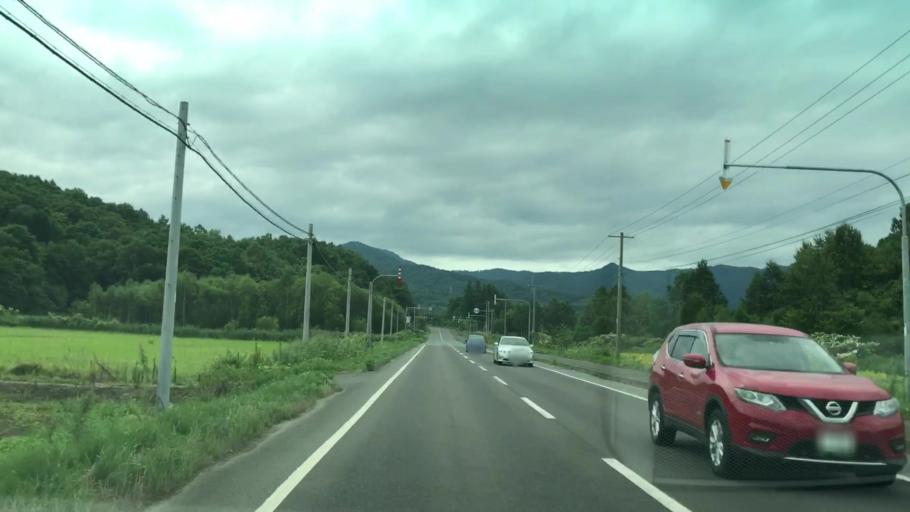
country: JP
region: Hokkaido
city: Yoichi
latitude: 43.0568
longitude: 140.8208
